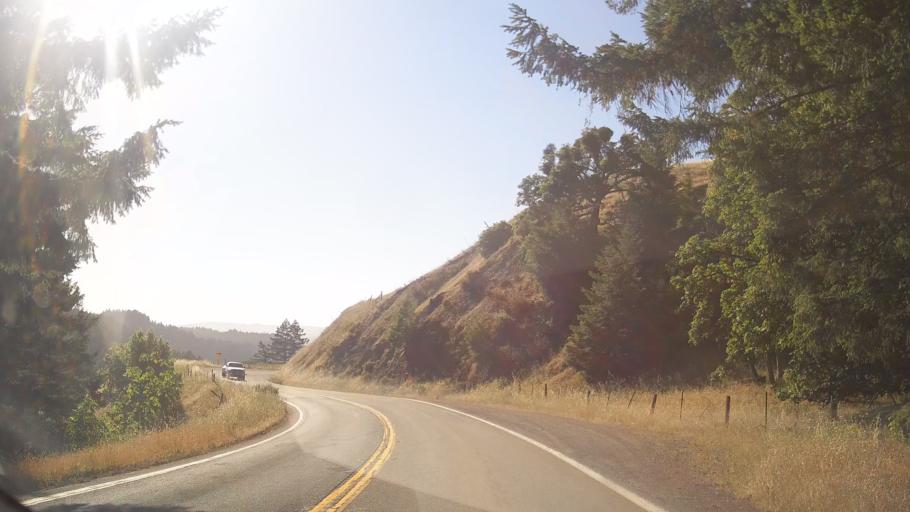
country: US
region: California
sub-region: Mendocino County
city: Brooktrails
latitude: 39.3904
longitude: -123.4446
